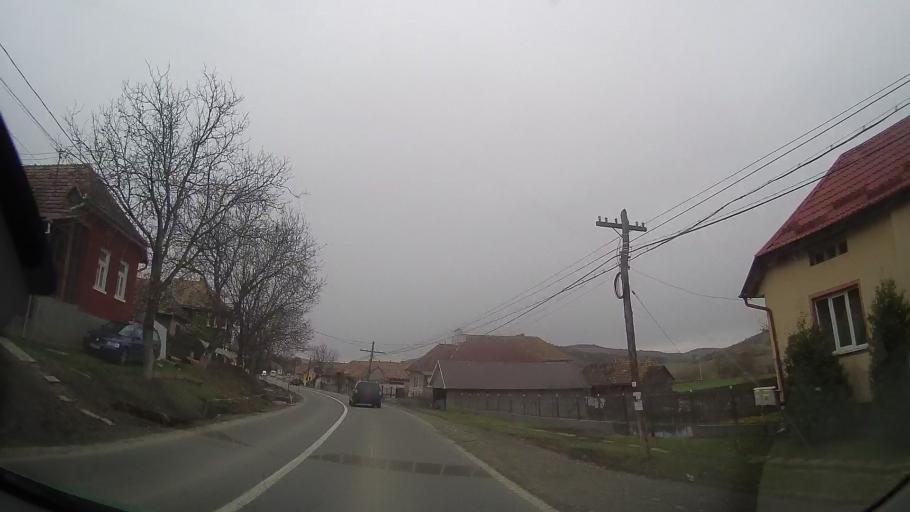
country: RO
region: Mures
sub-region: Comuna Ceausu de Campie
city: Ceausu de Campie
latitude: 46.6110
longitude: 24.5285
